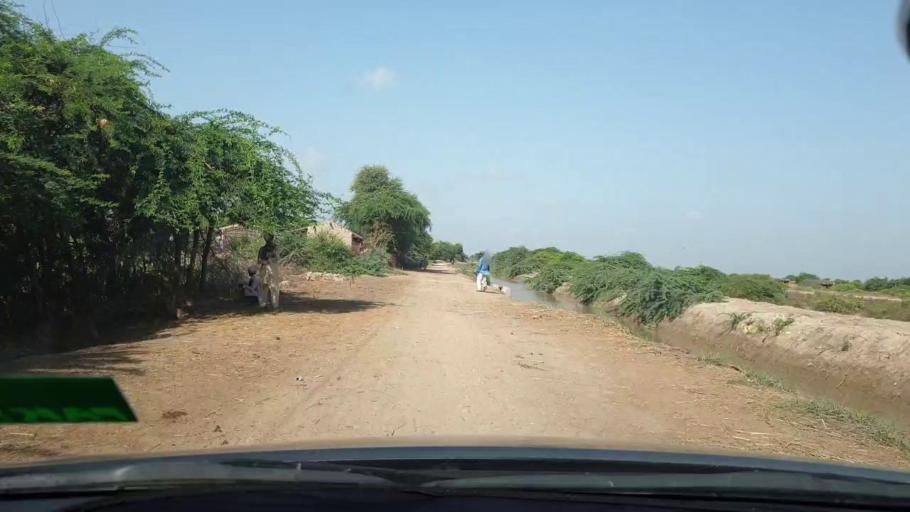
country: PK
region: Sindh
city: Tando Bago
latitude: 24.8758
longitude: 69.0107
